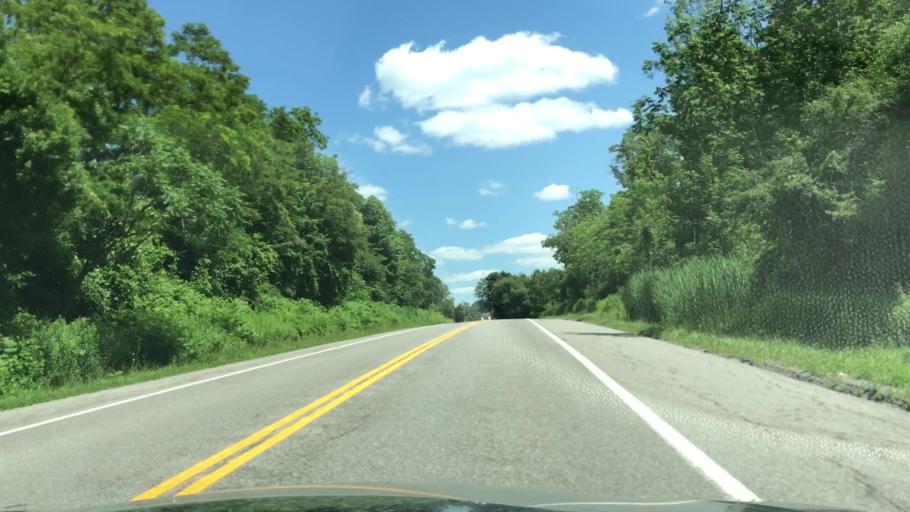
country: US
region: New York
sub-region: Erie County
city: Alden
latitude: 42.7706
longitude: -78.4763
